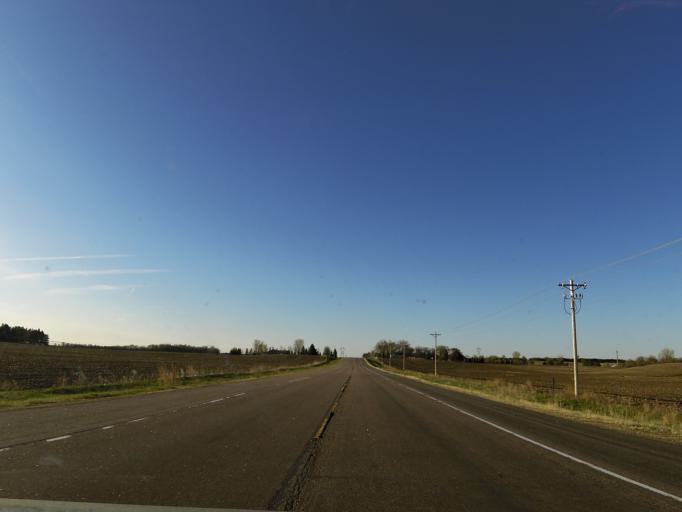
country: US
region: Wisconsin
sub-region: Pierce County
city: Prescott
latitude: 44.6180
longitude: -92.7725
